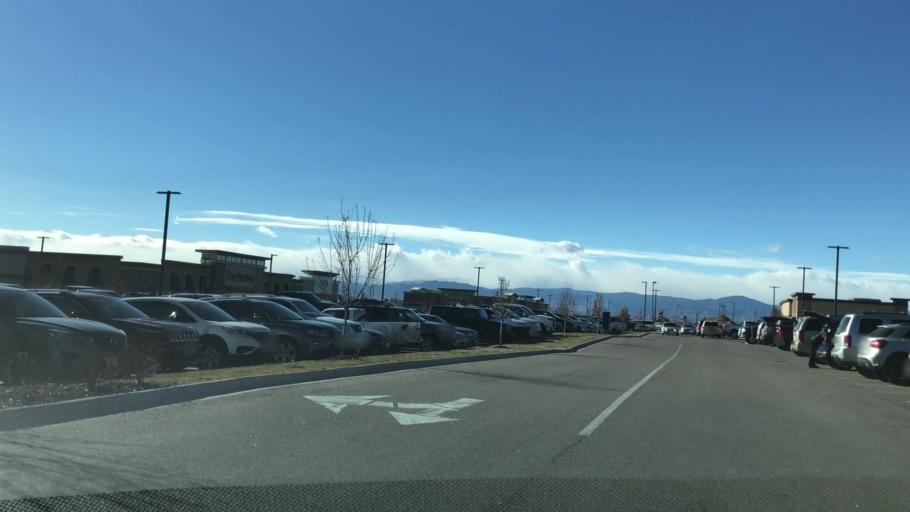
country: US
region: Colorado
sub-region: Larimer County
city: Loveland
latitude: 40.4052
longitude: -104.9803
